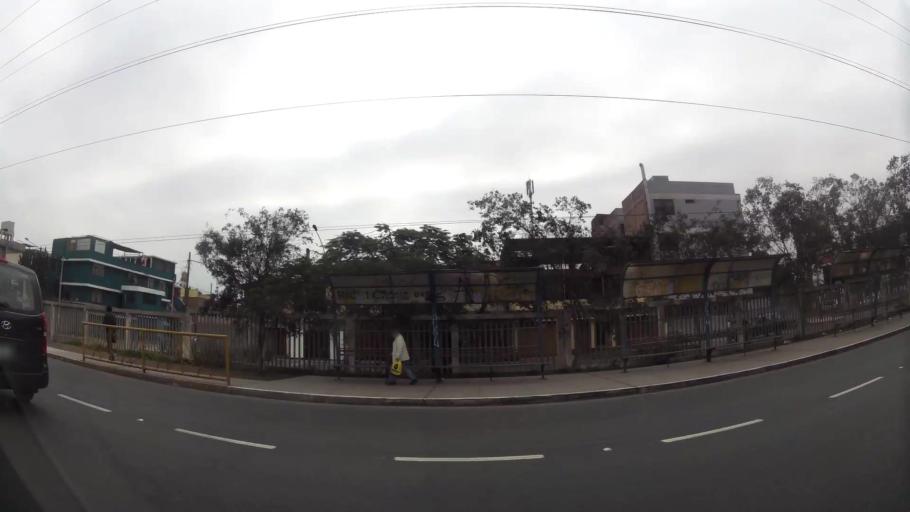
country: PE
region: Lima
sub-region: Lima
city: Surco
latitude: -12.1349
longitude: -76.9798
